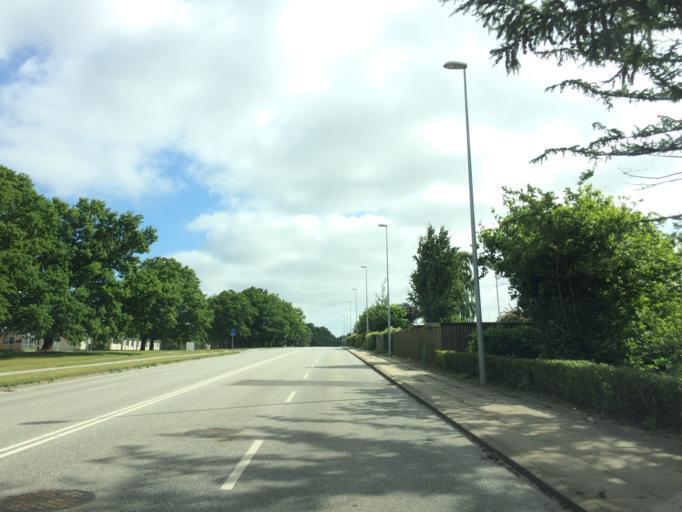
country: DK
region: Central Jutland
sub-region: Herning Kommune
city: Herning
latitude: 56.1434
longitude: 8.9451
